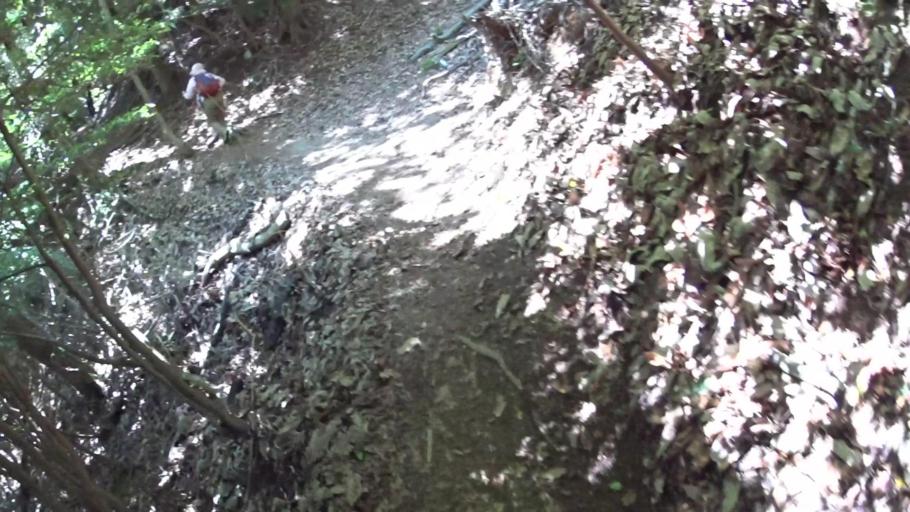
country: JP
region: Kyoto
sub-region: Kyoto-shi
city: Kamigyo-ku
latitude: 35.0543
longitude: 135.8161
